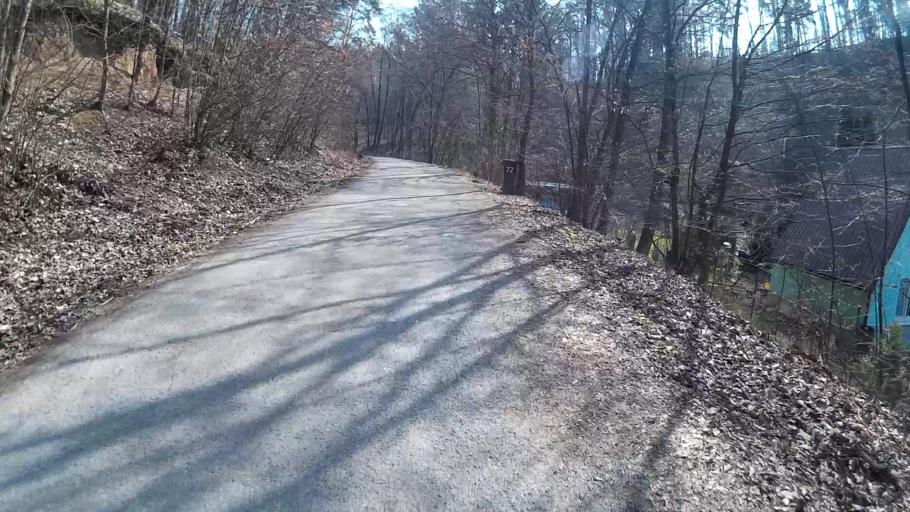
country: CZ
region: South Moravian
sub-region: Mesto Brno
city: Mokra Hora
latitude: 49.2568
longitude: 16.5975
